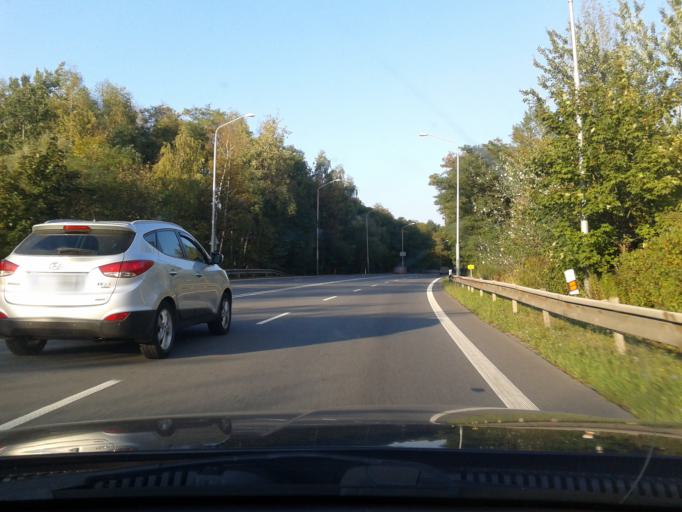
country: CZ
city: Senov
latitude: 49.8172
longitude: 18.3582
